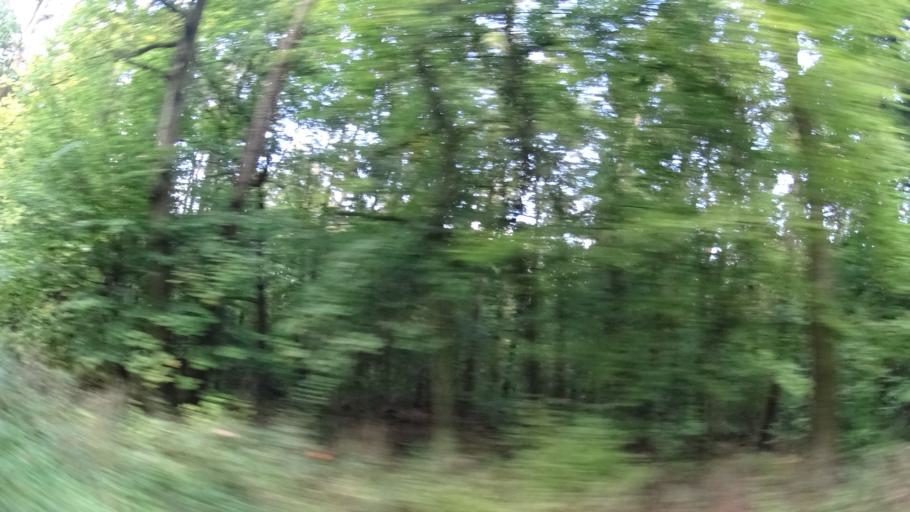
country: DE
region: Bavaria
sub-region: Regierungsbezirk Unterfranken
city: Frankenwinheim
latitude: 49.8634
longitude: 10.2777
